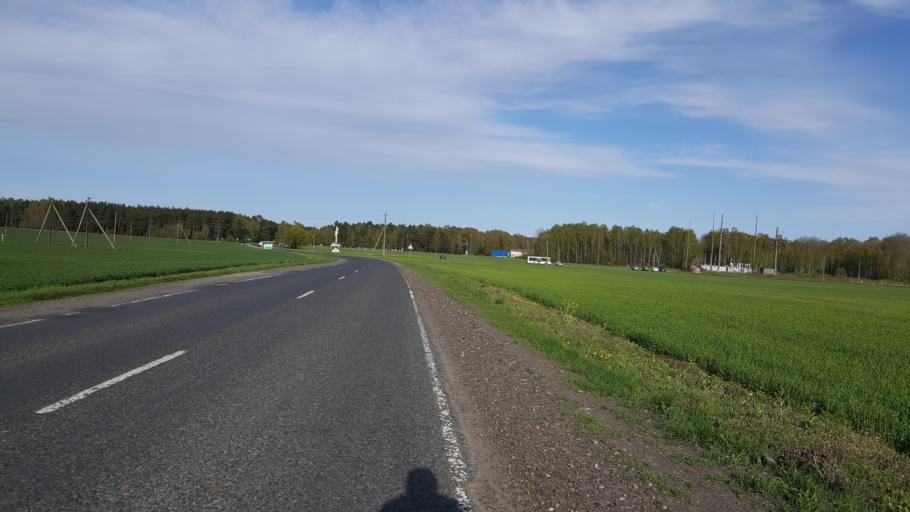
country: BY
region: Brest
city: Vysokaye
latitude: 52.3988
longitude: 23.4933
